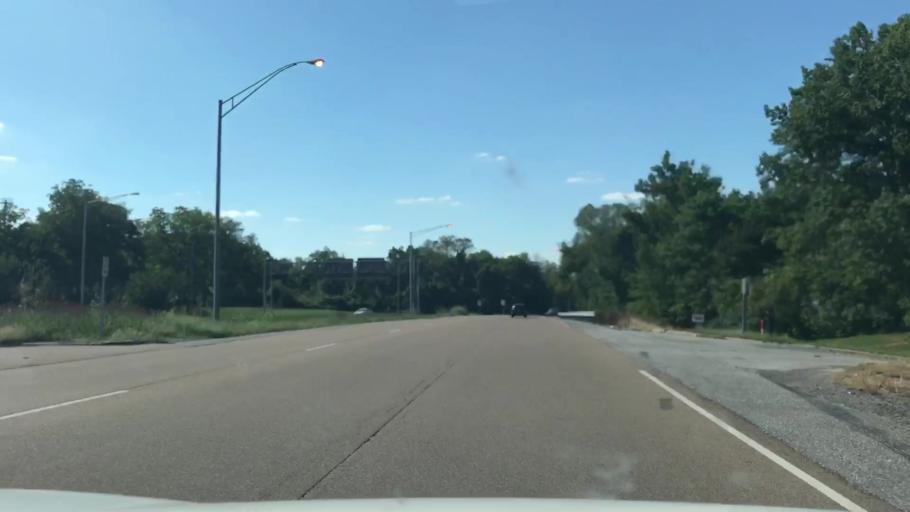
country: US
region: Illinois
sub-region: Saint Clair County
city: Alorton
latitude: 38.5503
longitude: -90.0698
